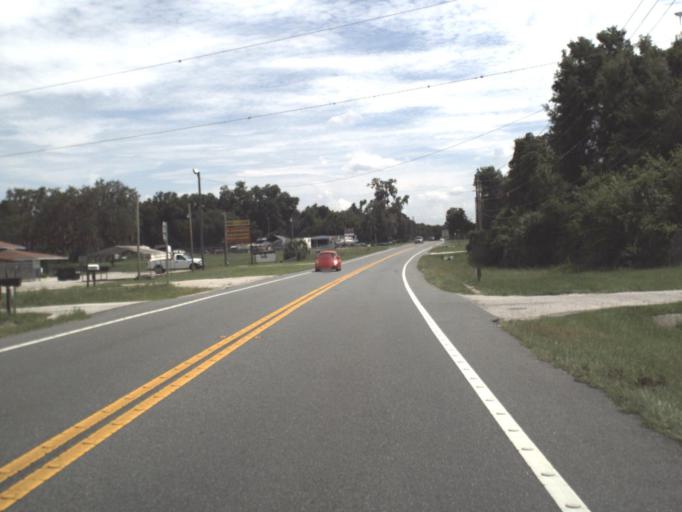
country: US
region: Florida
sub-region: Citrus County
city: Hernando
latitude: 28.9113
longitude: -82.3754
